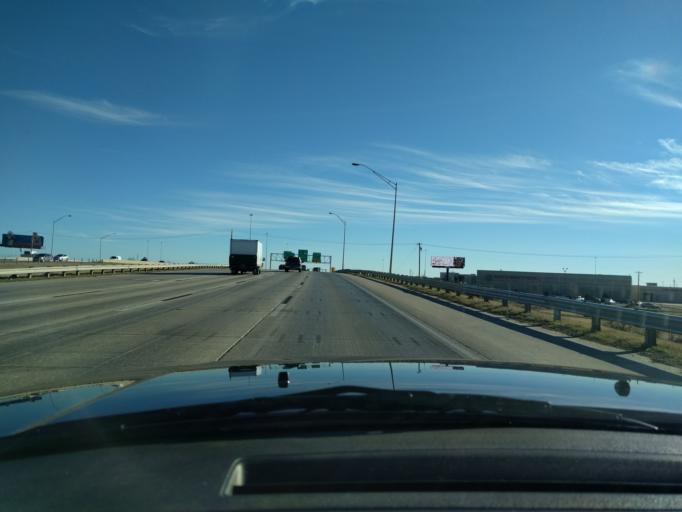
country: US
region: Oklahoma
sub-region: Oklahoma County
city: Oklahoma City
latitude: 35.4653
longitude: -97.5785
